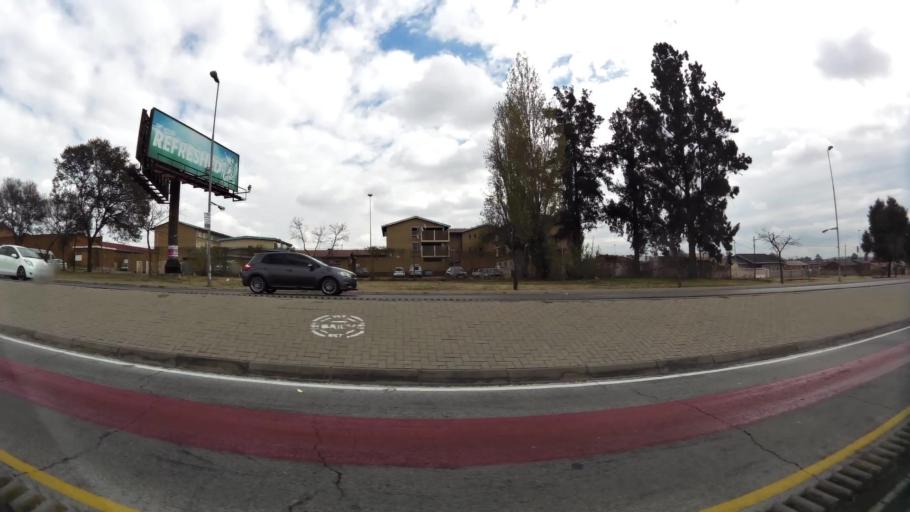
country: ZA
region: Gauteng
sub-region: City of Johannesburg Metropolitan Municipality
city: Soweto
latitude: -26.2676
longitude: 27.8768
